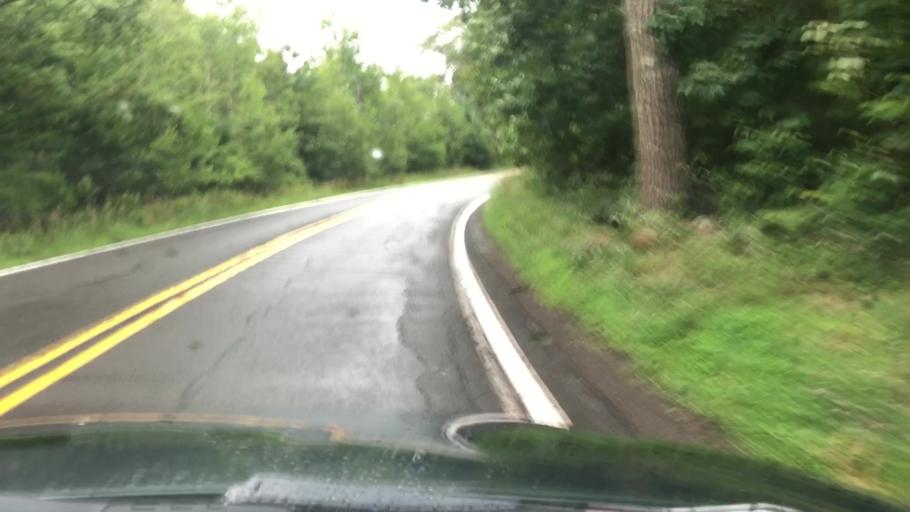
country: US
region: Pennsylvania
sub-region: Monroe County
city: Mountainhome
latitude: 41.2651
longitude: -75.2399
